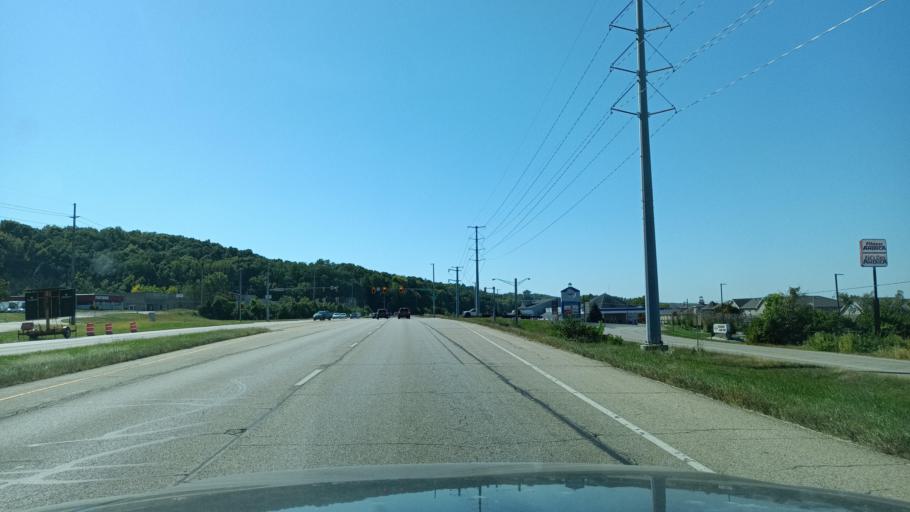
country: US
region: Illinois
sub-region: Peoria County
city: Peoria
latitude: 40.6962
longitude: -89.5406
